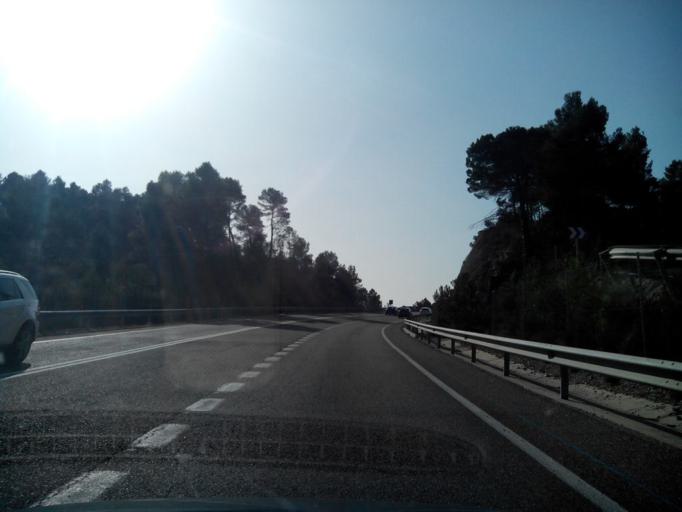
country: ES
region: Catalonia
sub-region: Provincia de Barcelona
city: Castellfollit del Boix
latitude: 41.6510
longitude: 1.7063
